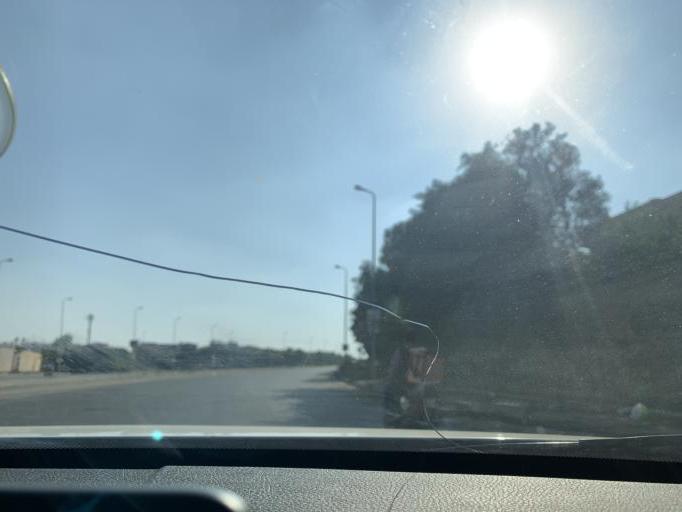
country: EG
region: Muhafazat al Qalyubiyah
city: Al Khankah
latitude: 30.0133
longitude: 31.4860
